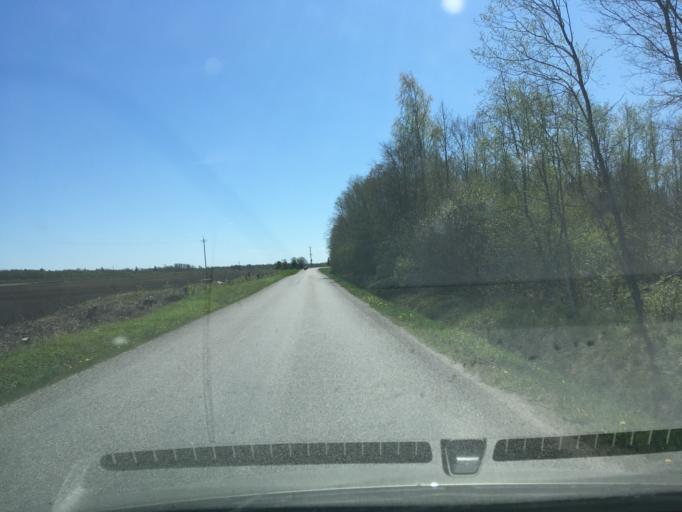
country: EE
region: Harju
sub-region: Raasiku vald
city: Arukula
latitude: 59.4013
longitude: 25.0786
